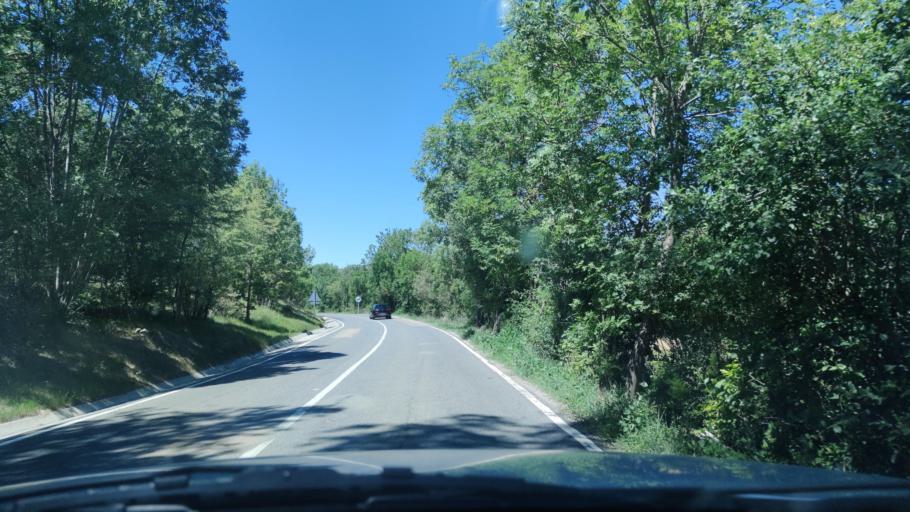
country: ES
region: Catalonia
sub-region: Provincia de Girona
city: Isovol
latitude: 42.3666
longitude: 1.8322
